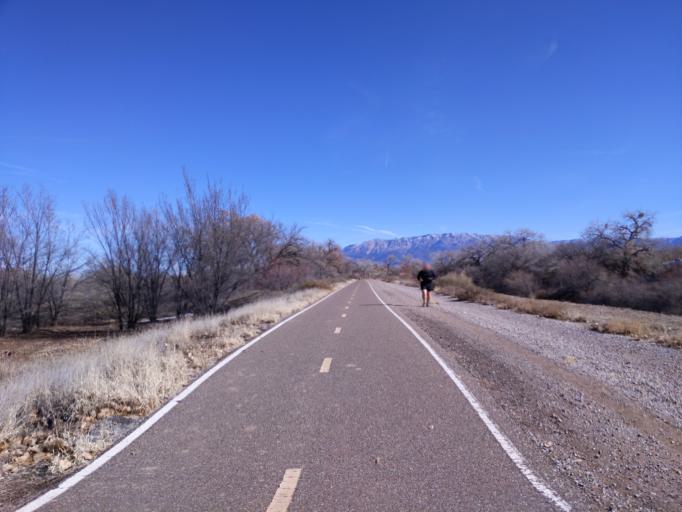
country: US
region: New Mexico
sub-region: Bernalillo County
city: Los Ranchos de Albuquerque
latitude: 35.1621
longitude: -106.6630
